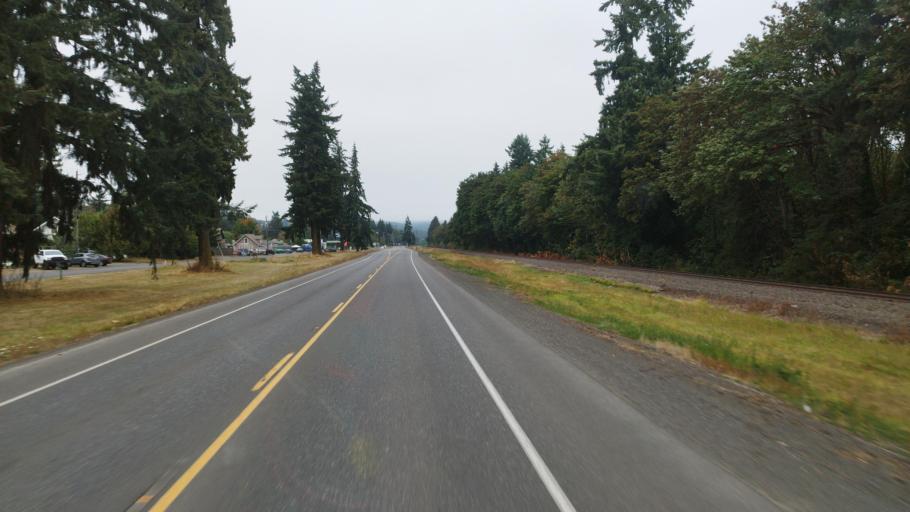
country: US
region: Oregon
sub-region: Columbia County
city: Columbia City
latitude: 45.9299
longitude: -122.8419
